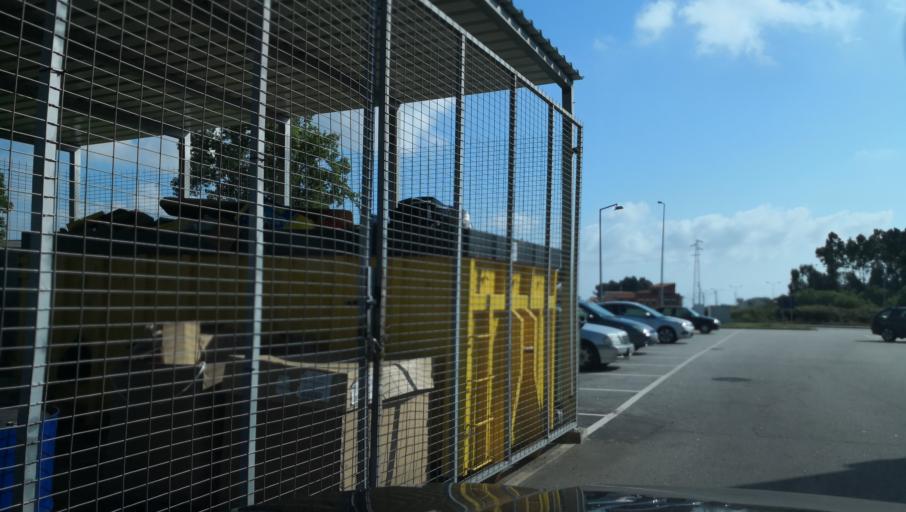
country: PT
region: Porto
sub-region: Matosinhos
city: Santa Cruz do Bispo
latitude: 41.2102
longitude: -8.6822
